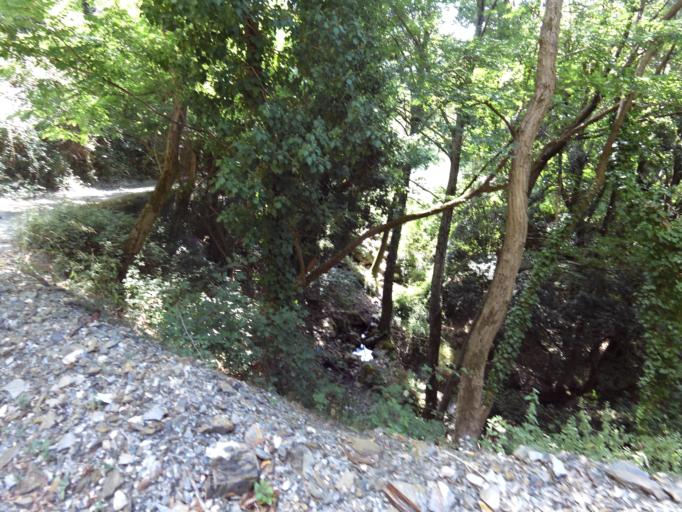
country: IT
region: Calabria
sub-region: Provincia di Reggio Calabria
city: Pazzano
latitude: 38.4683
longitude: 16.4308
